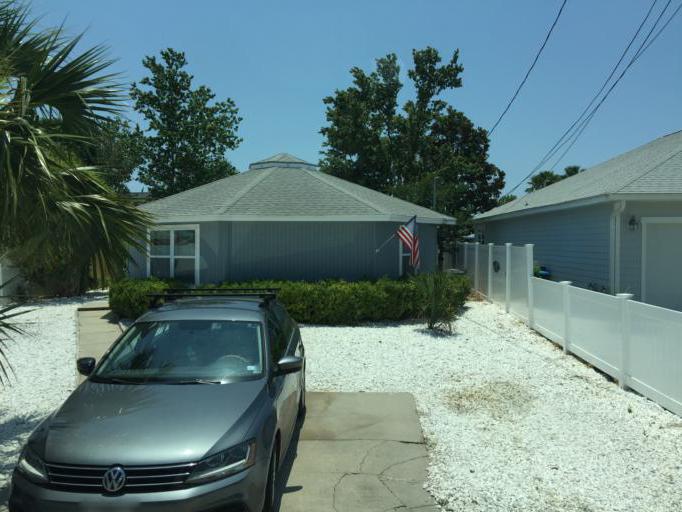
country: US
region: Florida
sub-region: Bay County
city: Panama City Beach
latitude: 30.2118
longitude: -85.8562
